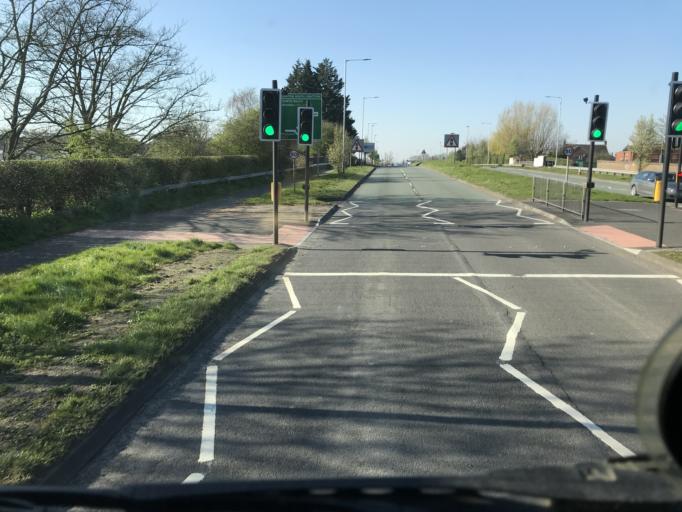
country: GB
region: England
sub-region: Cheshire West and Chester
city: Guilden Sutton
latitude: 53.1904
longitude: -2.8508
